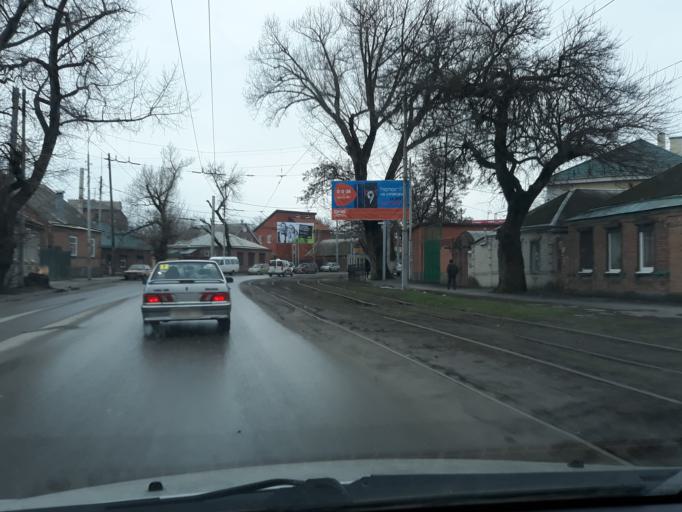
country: RU
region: Rostov
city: Taganrog
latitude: 47.2251
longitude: 38.9178
